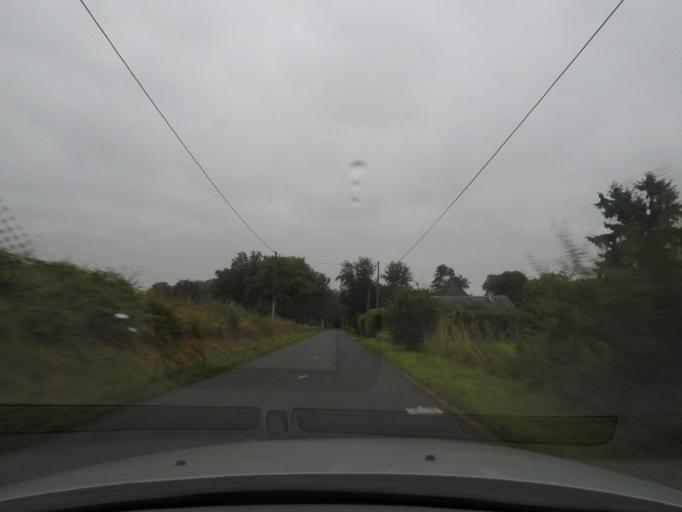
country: FR
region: Haute-Normandie
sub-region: Departement de la Seine-Maritime
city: Fontaine-le-Bourg
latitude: 49.5719
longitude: 1.1798
